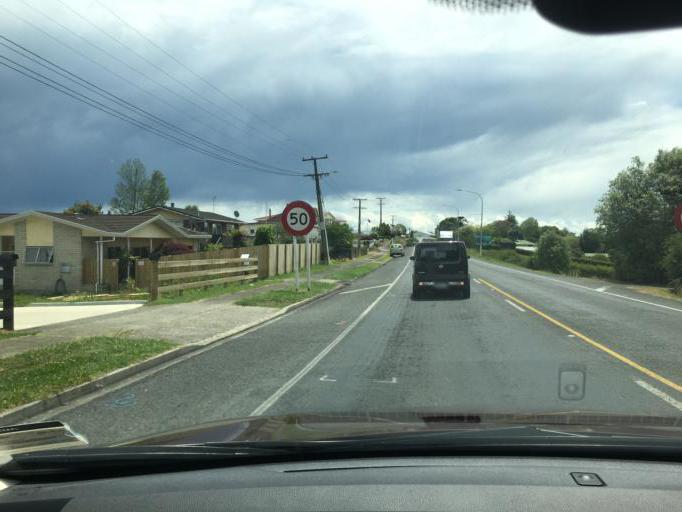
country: NZ
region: Waikato
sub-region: Waipa District
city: Cambridge
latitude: -37.9219
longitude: 175.3093
